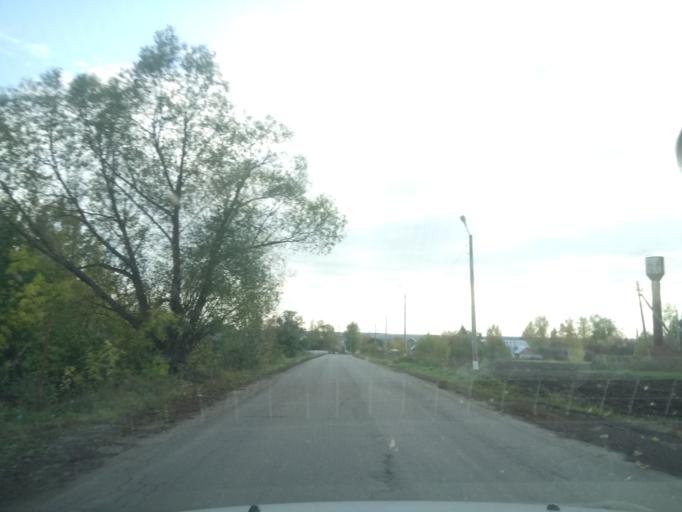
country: RU
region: Nizjnij Novgorod
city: Bol'shoye Boldino
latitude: 54.9977
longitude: 45.3160
